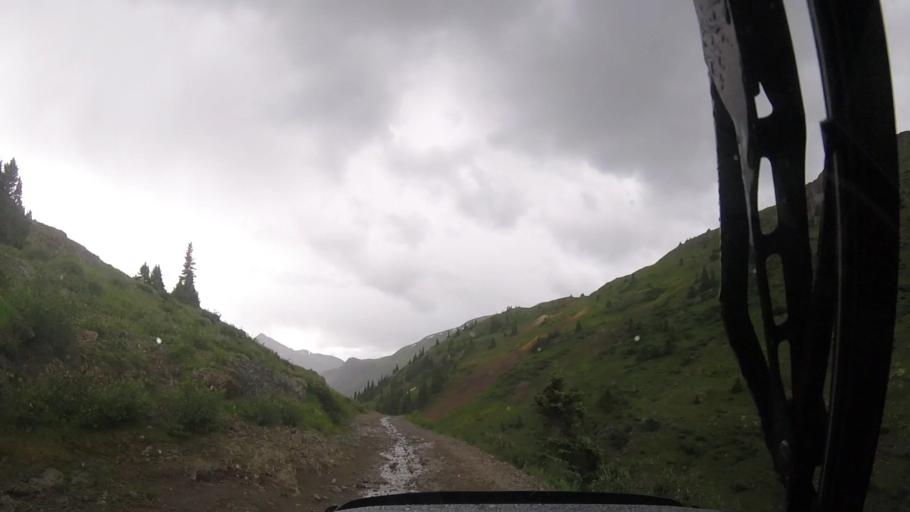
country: US
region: Colorado
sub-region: Ouray County
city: Ouray
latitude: 37.9403
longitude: -107.5737
